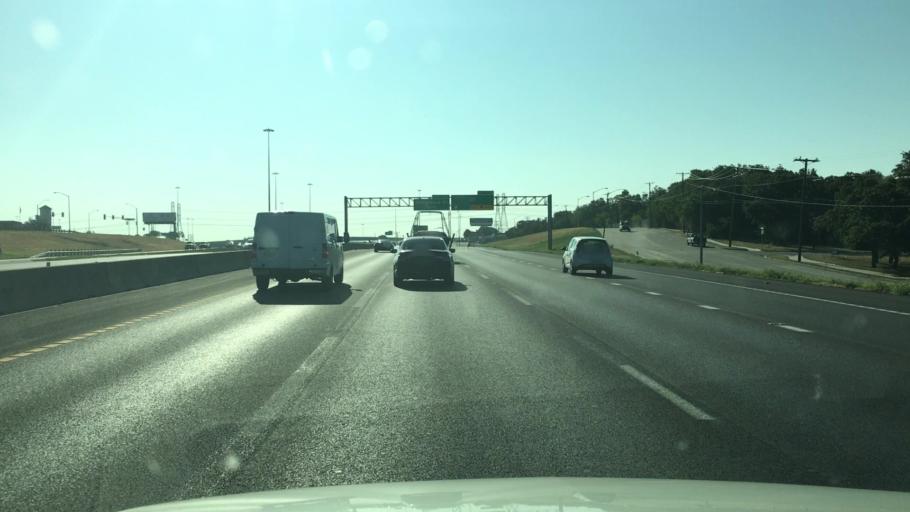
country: US
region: Texas
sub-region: Tarrant County
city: Richland Hills
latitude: 32.7599
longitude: -97.2270
